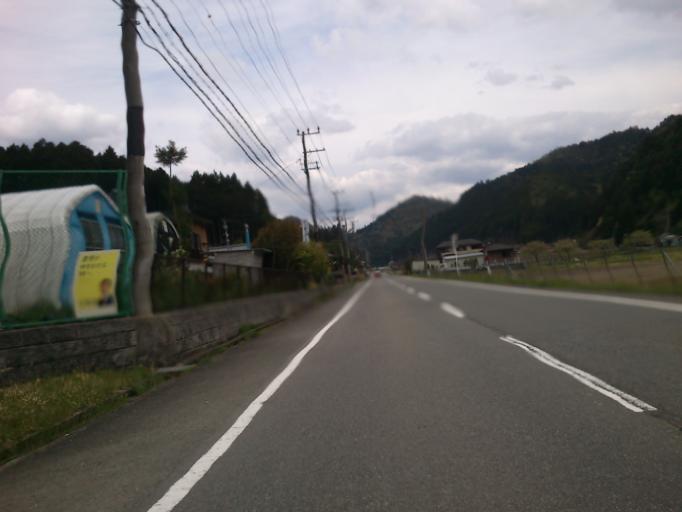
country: JP
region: Kyoto
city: Kameoka
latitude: 35.2071
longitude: 135.6021
